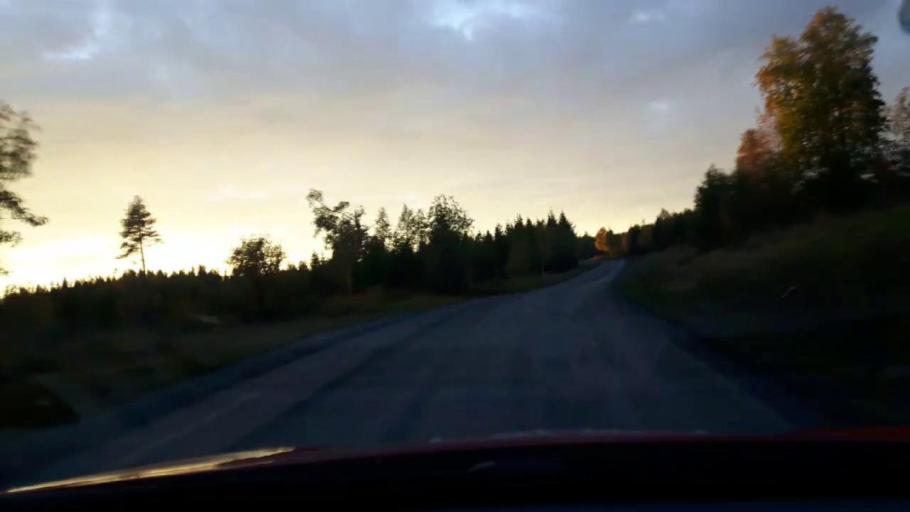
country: SE
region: Jaemtland
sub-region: OEstersunds Kommun
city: Lit
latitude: 63.2886
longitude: 14.8534
